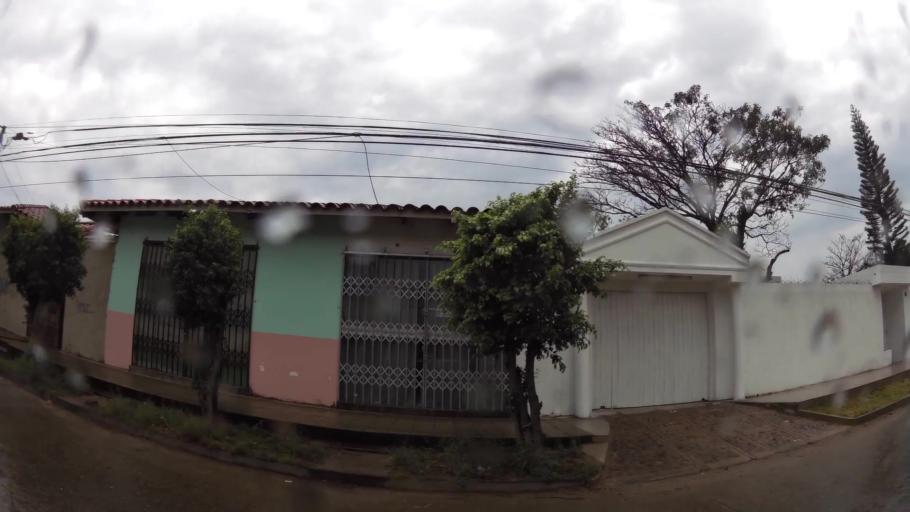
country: BO
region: Santa Cruz
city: Santa Cruz de la Sierra
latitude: -17.8037
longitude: -63.1569
